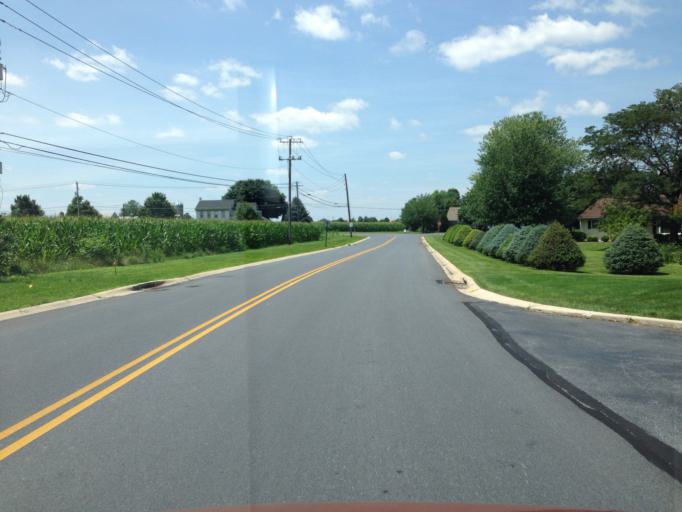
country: US
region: Pennsylvania
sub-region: Lancaster County
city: East Petersburg
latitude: 40.1179
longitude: -76.3174
